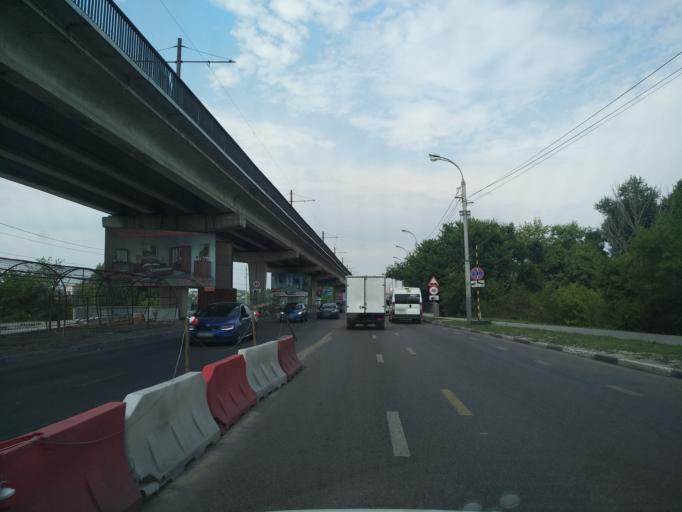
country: RU
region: Voronezj
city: Voronezh
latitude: 51.6892
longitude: 39.2500
